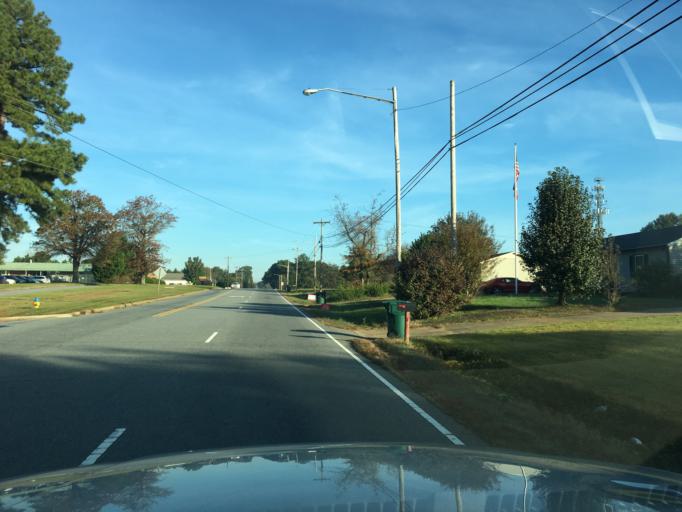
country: US
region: North Carolina
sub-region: Catawba County
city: Newton
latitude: 35.6375
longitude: -81.2679
